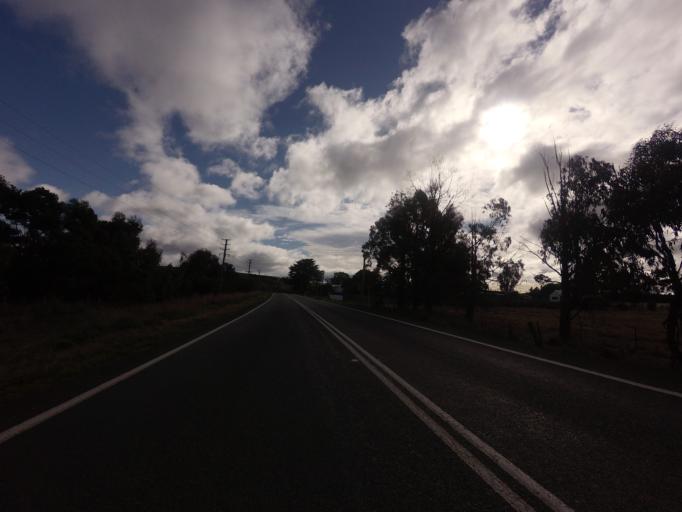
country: AU
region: Tasmania
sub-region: Derwent Valley
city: New Norfolk
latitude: -42.6745
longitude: 146.9343
